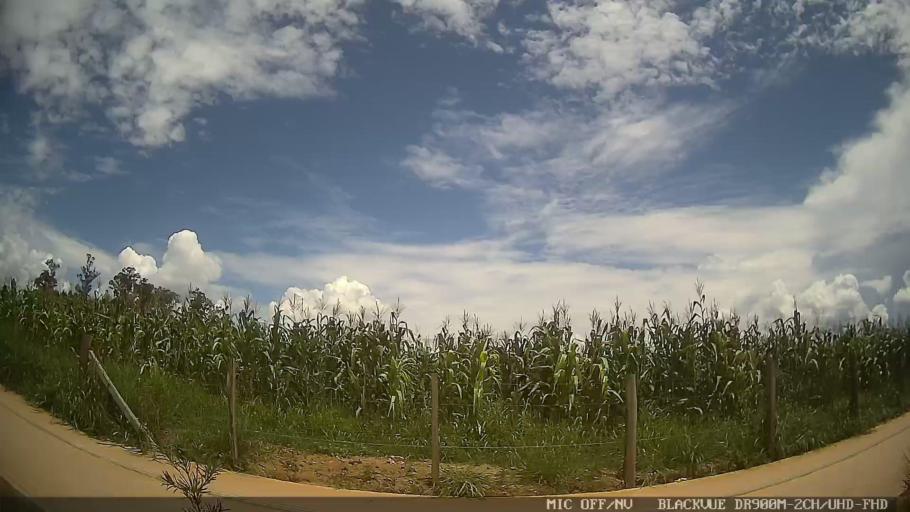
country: BR
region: Sao Paulo
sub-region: Conchas
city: Conchas
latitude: -23.0870
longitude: -47.9792
